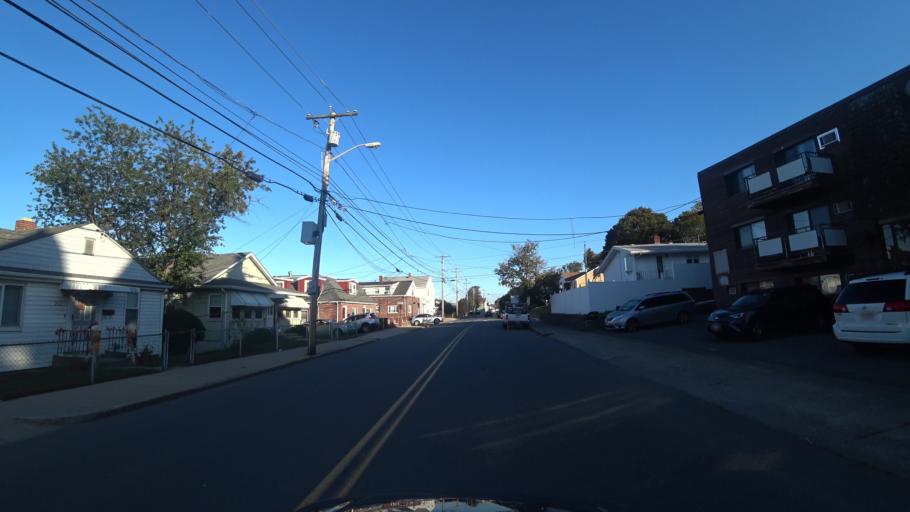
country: US
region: Massachusetts
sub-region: Suffolk County
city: Revere
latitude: 42.4200
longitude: -71.0140
